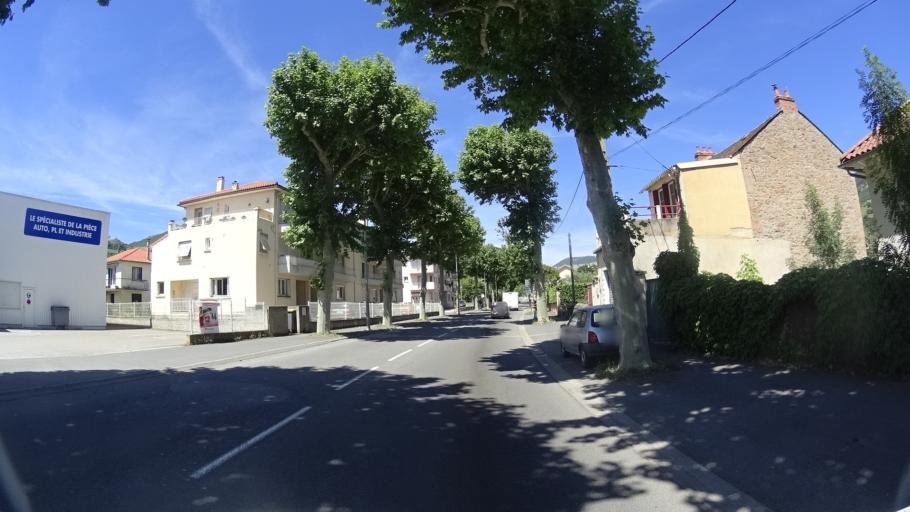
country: FR
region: Midi-Pyrenees
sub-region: Departement de l'Aveyron
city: Millau
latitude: 44.1139
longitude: 3.0829
